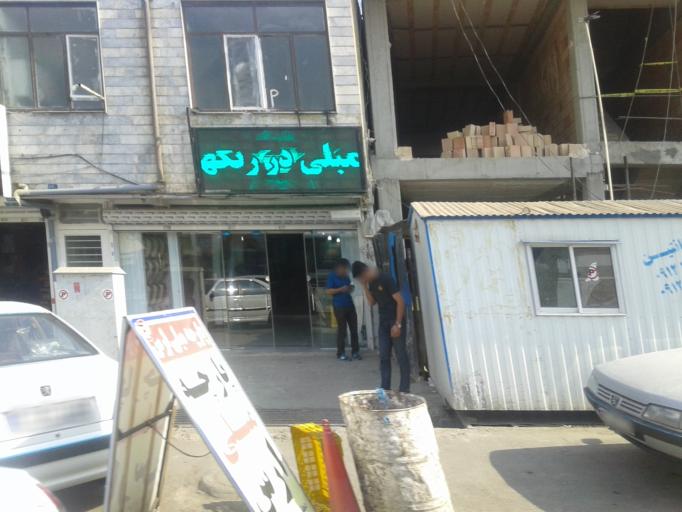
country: IR
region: Tehran
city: Tehran
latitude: 35.6530
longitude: 51.3124
